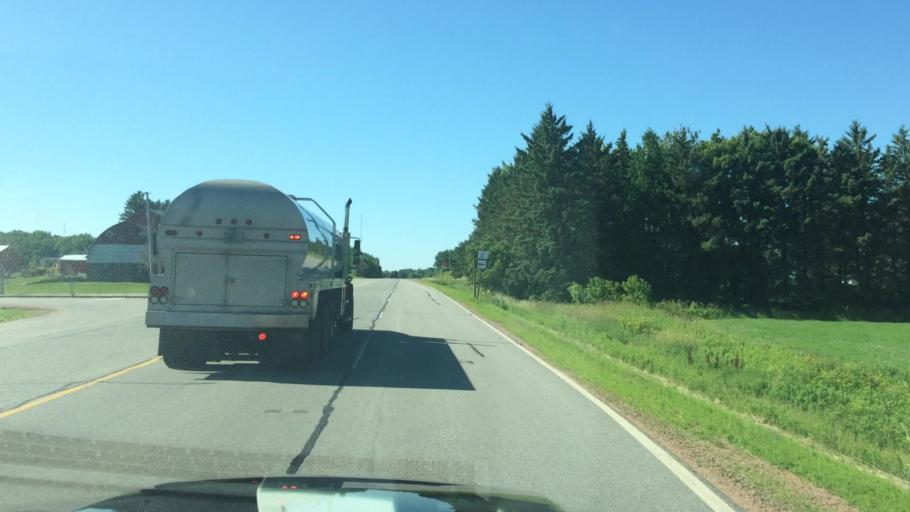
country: US
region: Wisconsin
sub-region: Marathon County
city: Stratford
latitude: 44.7435
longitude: -90.0794
